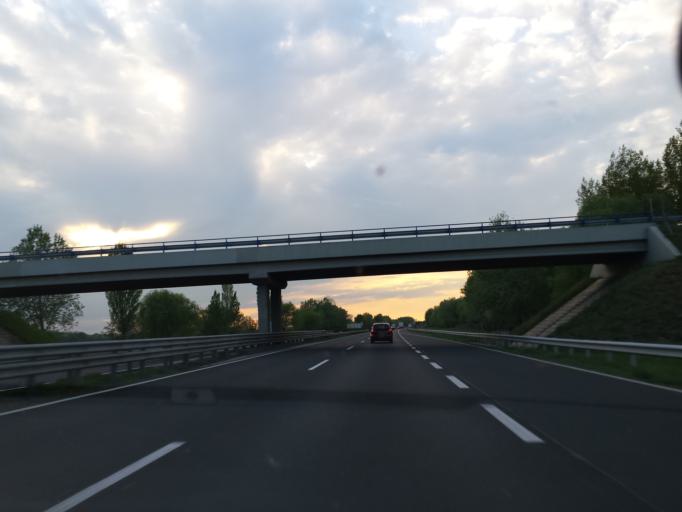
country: HU
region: Gyor-Moson-Sopron
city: Kimle
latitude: 47.7923
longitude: 17.3228
